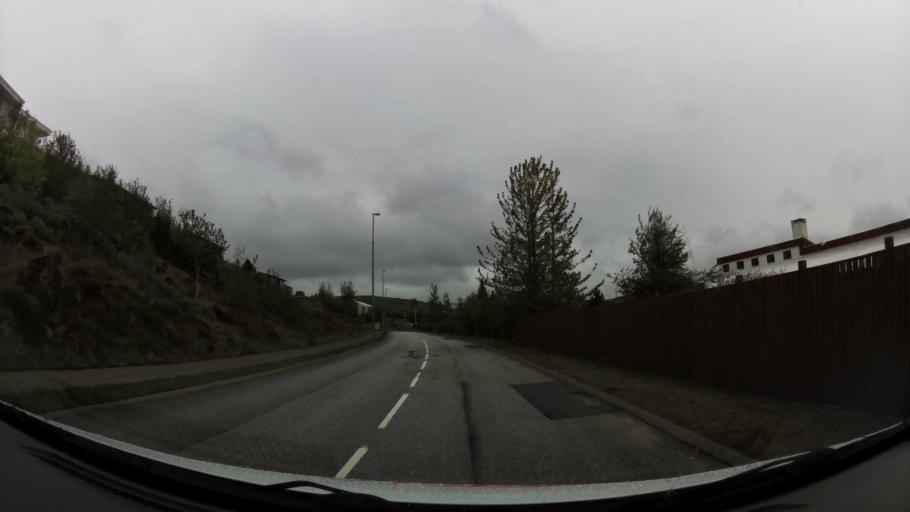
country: IS
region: Capital Region
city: Hafnarfjoerdur
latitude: 64.0611
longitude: -21.9247
